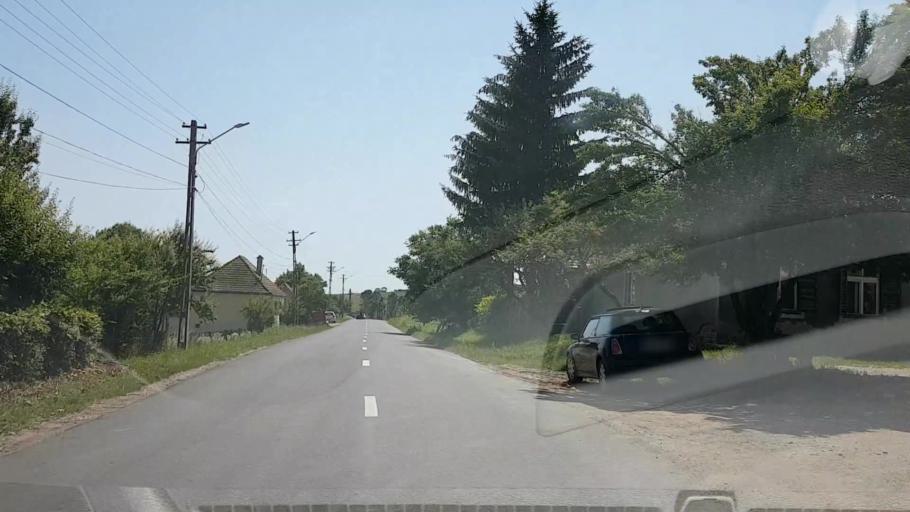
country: RO
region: Sibiu
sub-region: Comuna Merghindeal
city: Merghindeal
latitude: 45.9634
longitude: 24.7344
